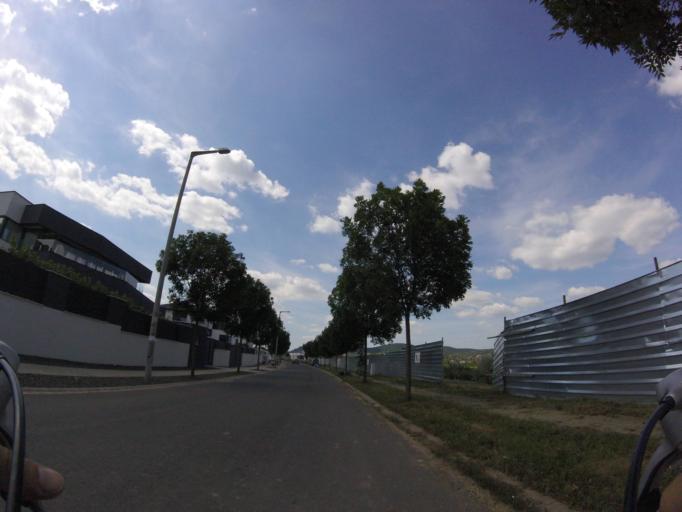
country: HU
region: Pest
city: Toeroekbalint
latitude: 47.4418
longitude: 18.9299
